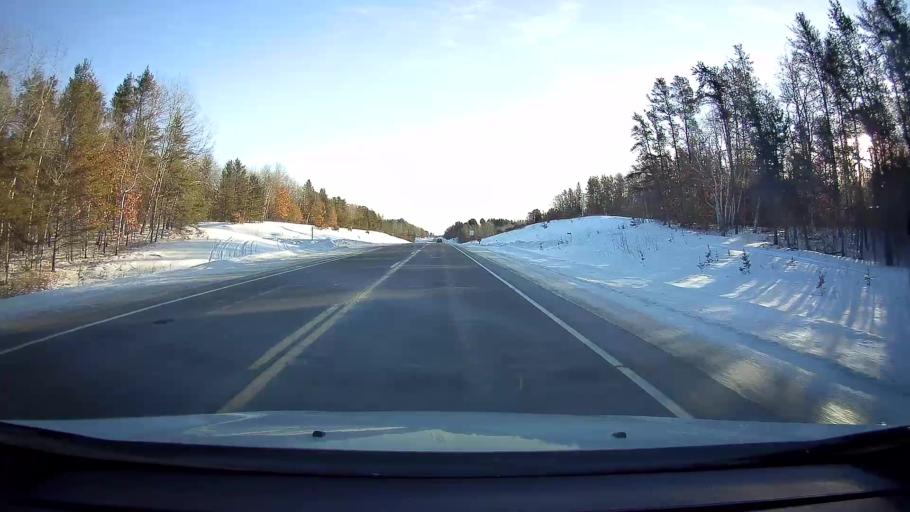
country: US
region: Wisconsin
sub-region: Washburn County
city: Spooner
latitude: 45.9104
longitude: -91.7876
